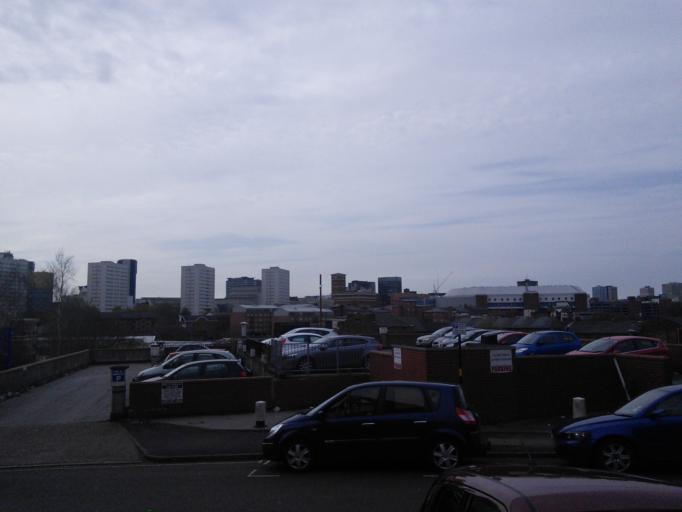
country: GB
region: England
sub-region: City and Borough of Birmingham
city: Birmingham
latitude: 52.4843
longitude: -1.9121
